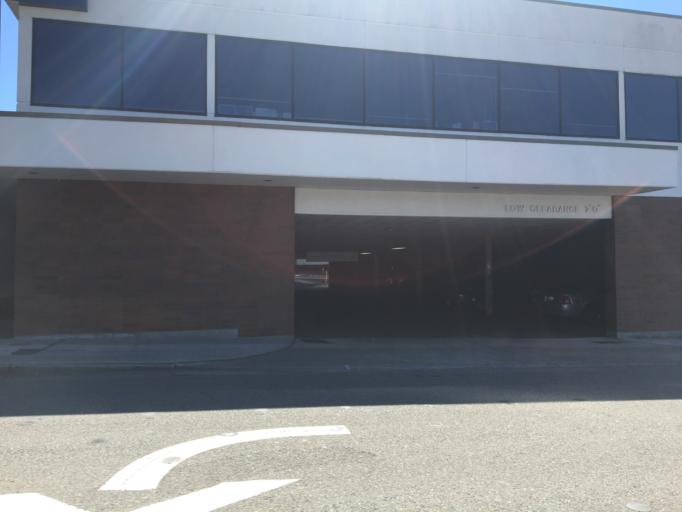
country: US
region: Washington
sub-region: King County
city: Bellevue
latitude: 47.6136
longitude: -122.1989
